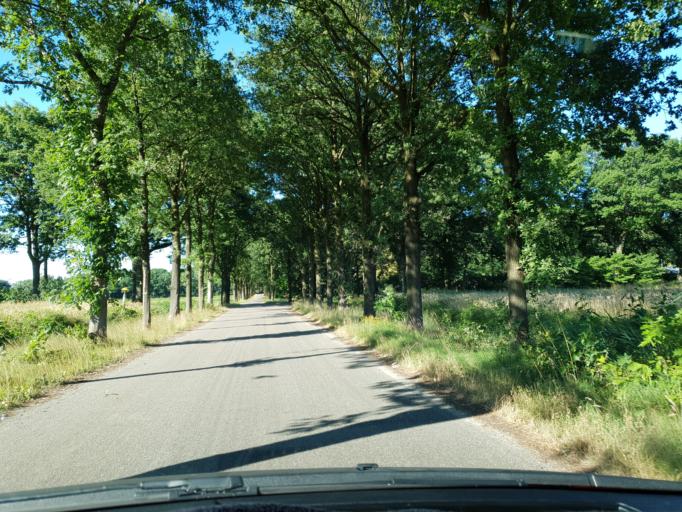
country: NL
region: North Brabant
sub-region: Gemeente Zundert
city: Zundert
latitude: 51.4948
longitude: 4.6051
